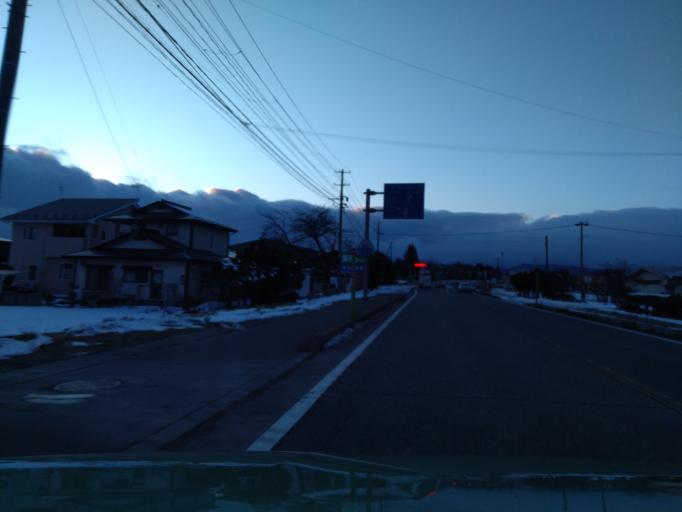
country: JP
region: Iwate
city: Shizukuishi
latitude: 39.6890
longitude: 140.9951
